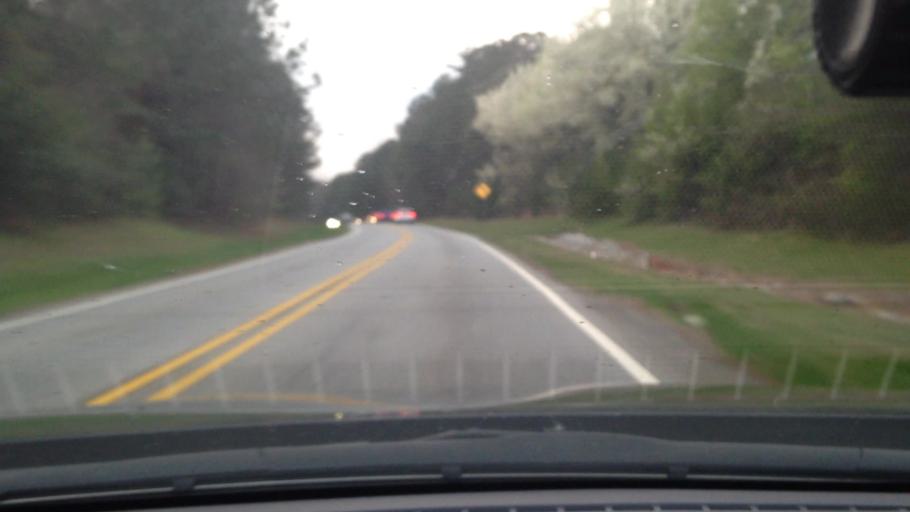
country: US
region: Georgia
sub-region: Coweta County
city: East Newnan
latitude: 33.3775
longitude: -84.7182
